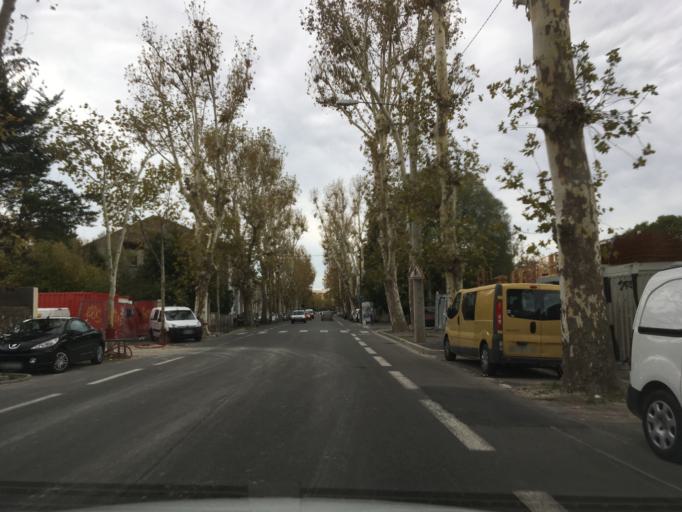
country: FR
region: Languedoc-Roussillon
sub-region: Departement de l'Herault
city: Montpellier
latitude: 43.6196
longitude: 3.8868
